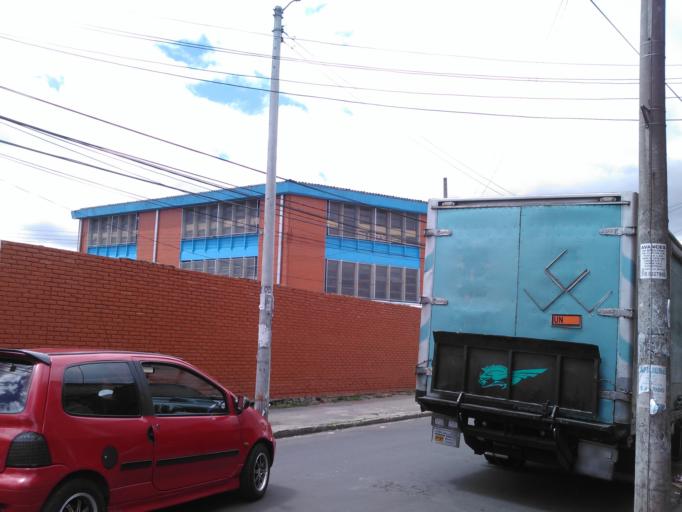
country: CO
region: Bogota D.C.
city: Bogota
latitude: 4.6168
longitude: -74.1225
